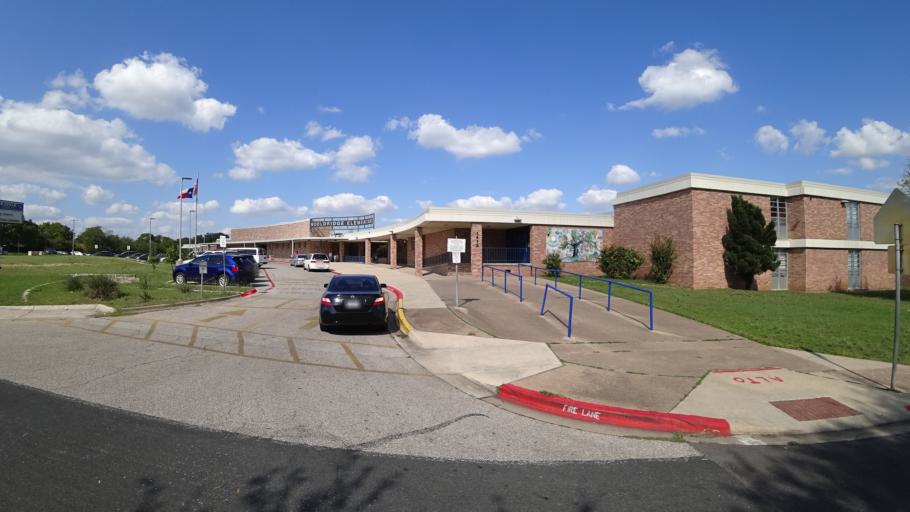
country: US
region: Texas
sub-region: Travis County
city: Wells Branch
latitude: 30.3643
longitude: -97.7100
